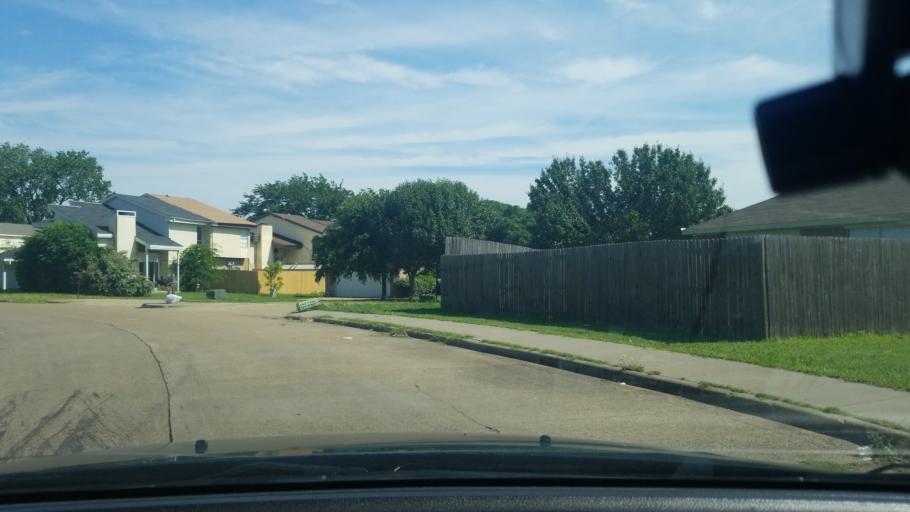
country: US
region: Texas
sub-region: Dallas County
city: Mesquite
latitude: 32.7791
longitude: -96.5956
